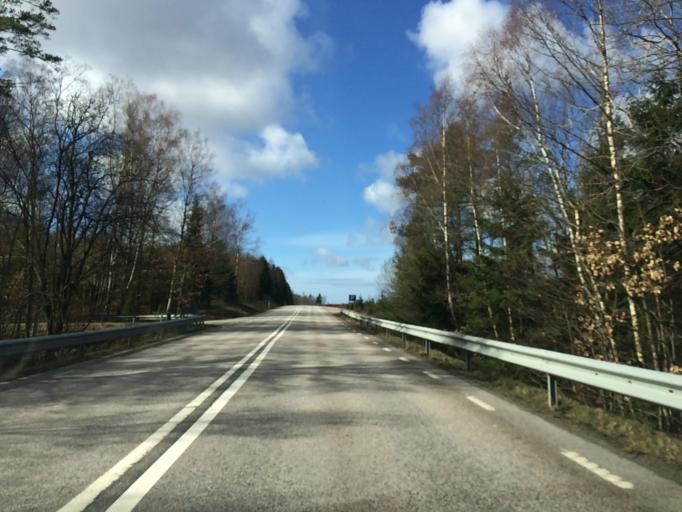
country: SE
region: Halland
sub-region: Laholms Kommun
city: Knared
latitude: 56.4982
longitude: 13.3754
